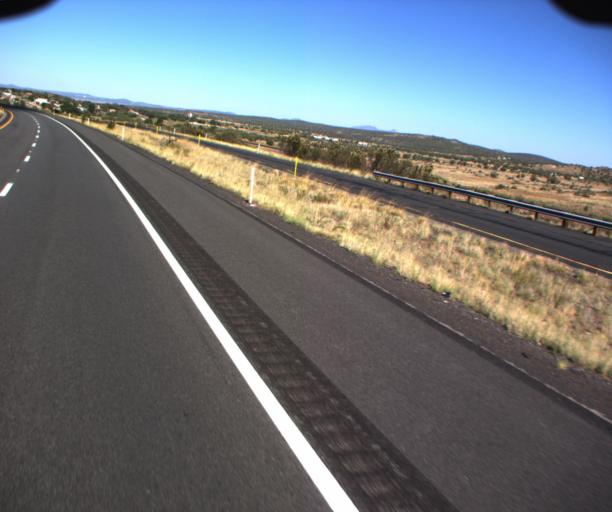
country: US
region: Arizona
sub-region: Coconino County
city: Williams
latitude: 35.2216
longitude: -112.4671
